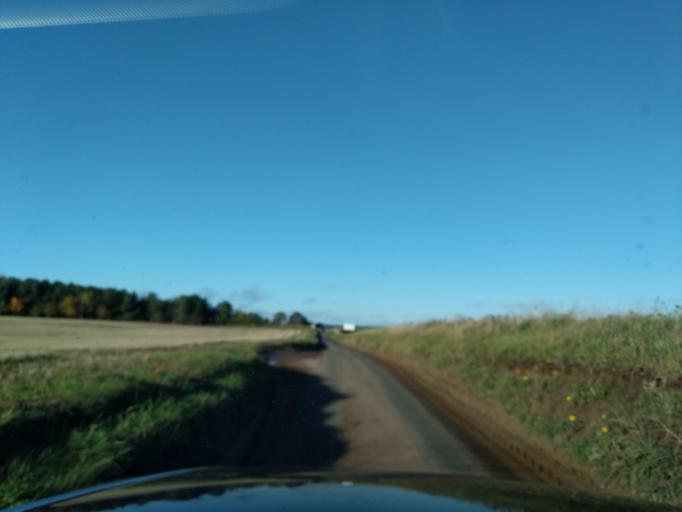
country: GB
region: Scotland
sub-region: Fife
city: Leuchars
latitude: 56.3978
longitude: -2.8651
